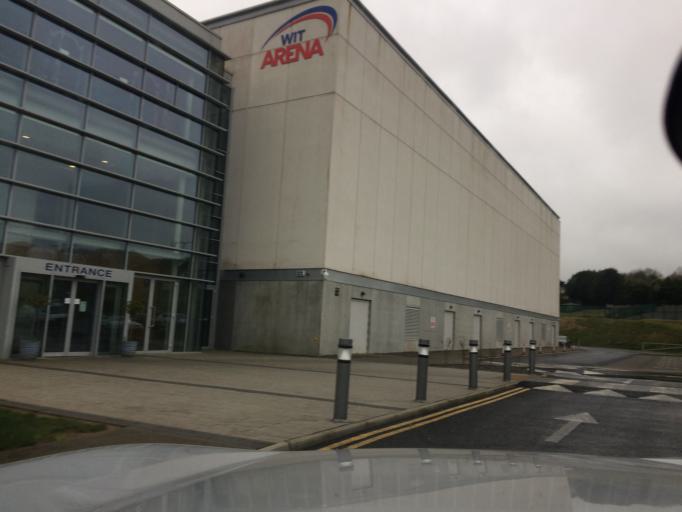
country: IE
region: Munster
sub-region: Waterford
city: Waterford
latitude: 52.2520
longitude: -7.1795
